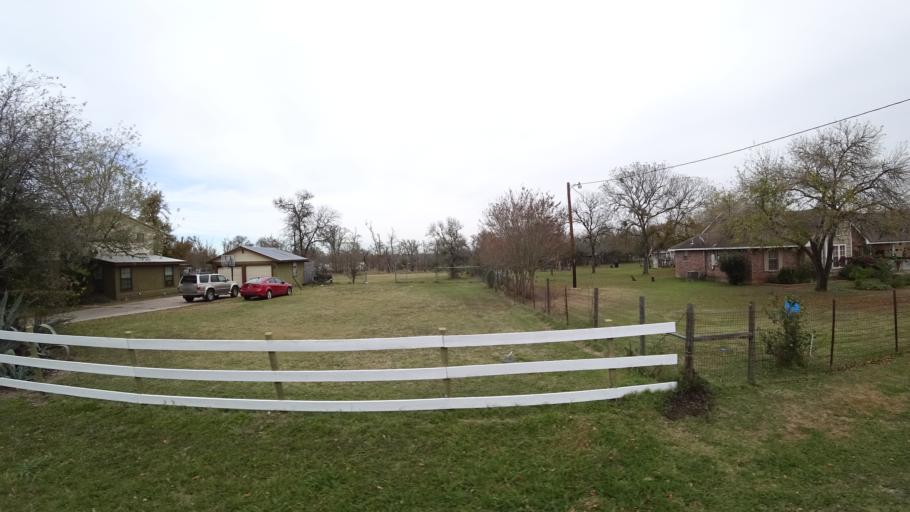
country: US
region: Texas
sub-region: Travis County
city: Garfield
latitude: 30.1068
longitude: -97.5743
